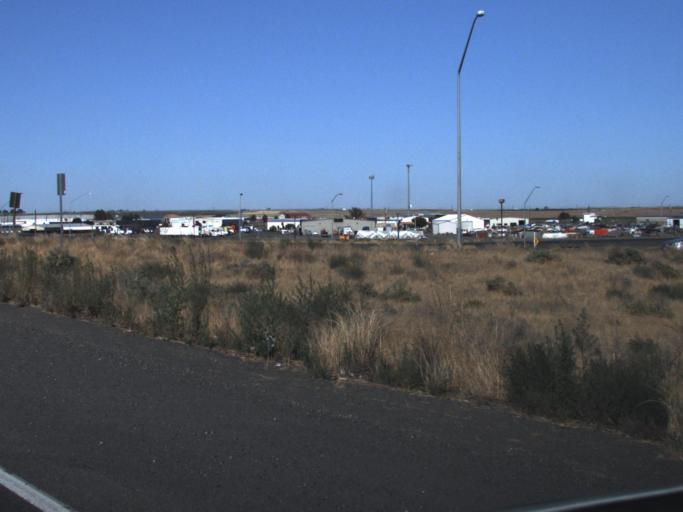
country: US
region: Washington
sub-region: Franklin County
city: Pasco
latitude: 46.2503
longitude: -119.0823
